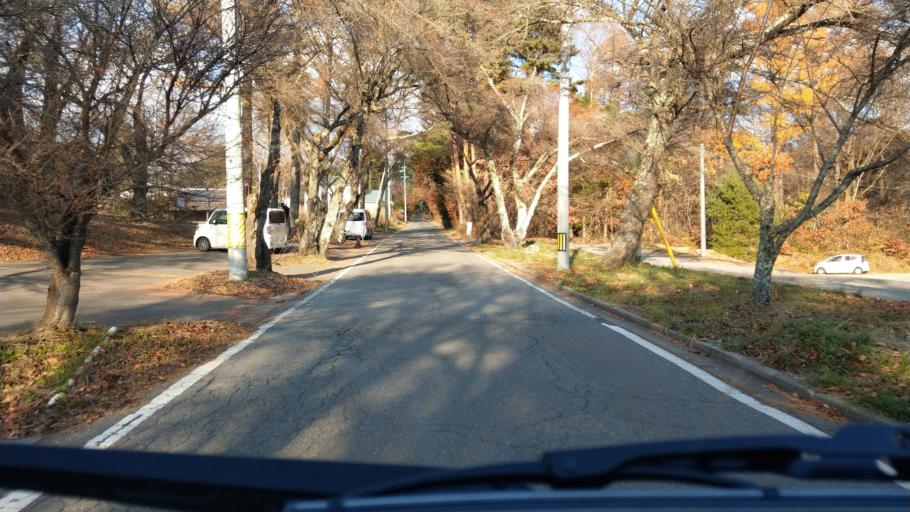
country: JP
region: Nagano
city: Komoro
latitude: 36.3486
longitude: 138.4569
